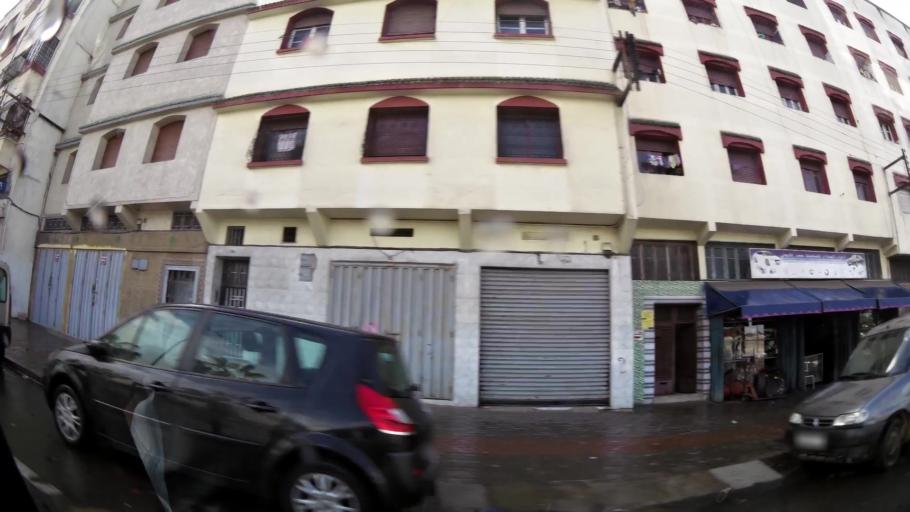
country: MA
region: Grand Casablanca
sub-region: Casablanca
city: Casablanca
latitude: 33.5458
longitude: -7.5636
